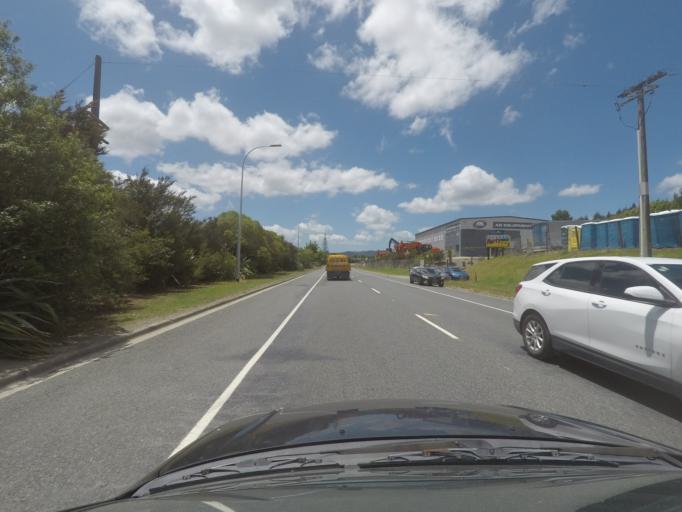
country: NZ
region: Northland
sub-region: Whangarei
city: Whangarei
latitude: -35.7456
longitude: 174.3230
